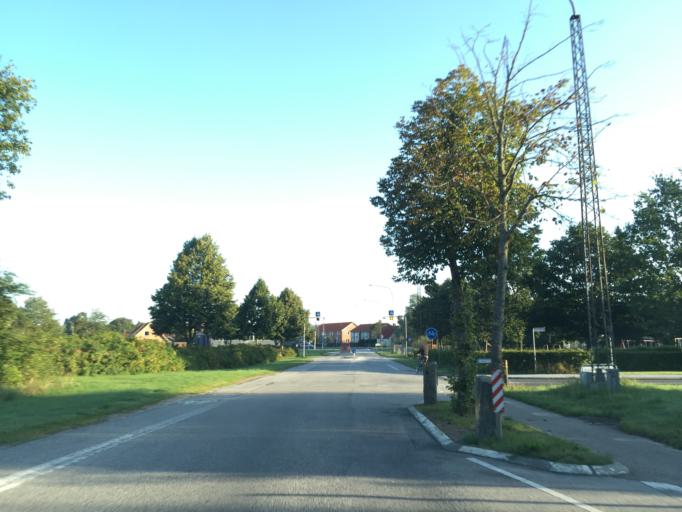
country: DK
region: Central Jutland
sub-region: Viborg Kommune
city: Bjerringbro
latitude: 56.3644
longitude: 9.6632
